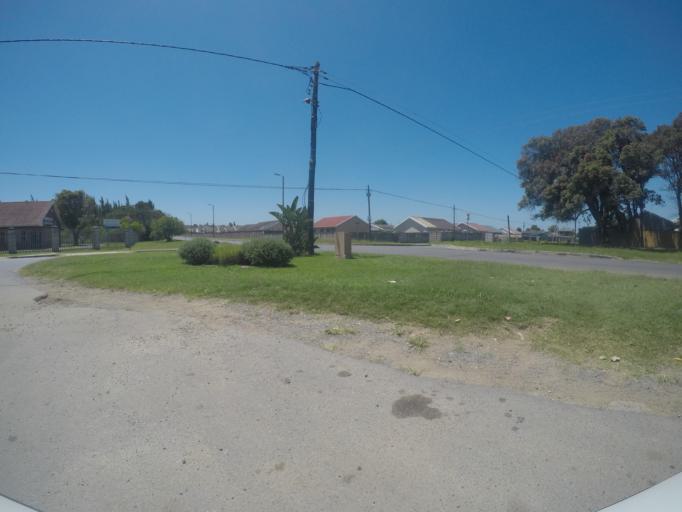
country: ZA
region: Eastern Cape
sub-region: Buffalo City Metropolitan Municipality
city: East London
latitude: -32.9506
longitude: 27.9972
